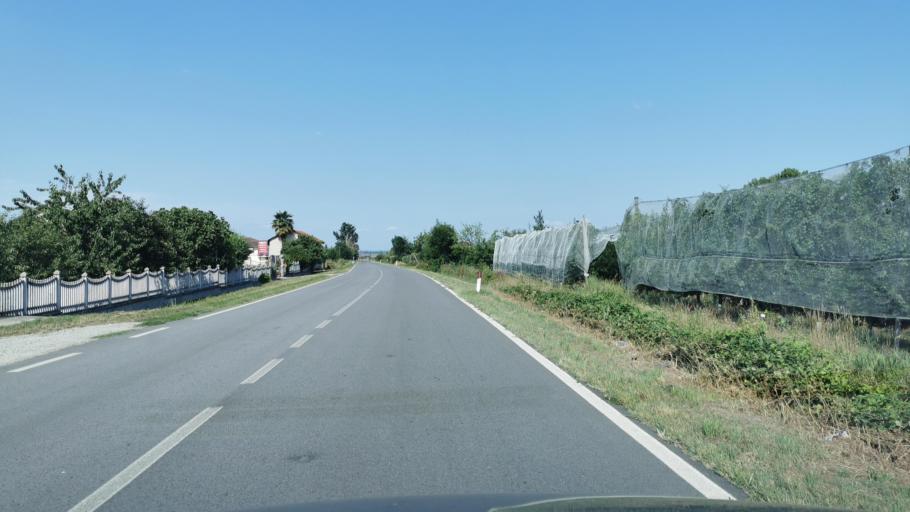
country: IT
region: Piedmont
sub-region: Provincia di Cuneo
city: Revello
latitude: 44.6726
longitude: 7.4028
